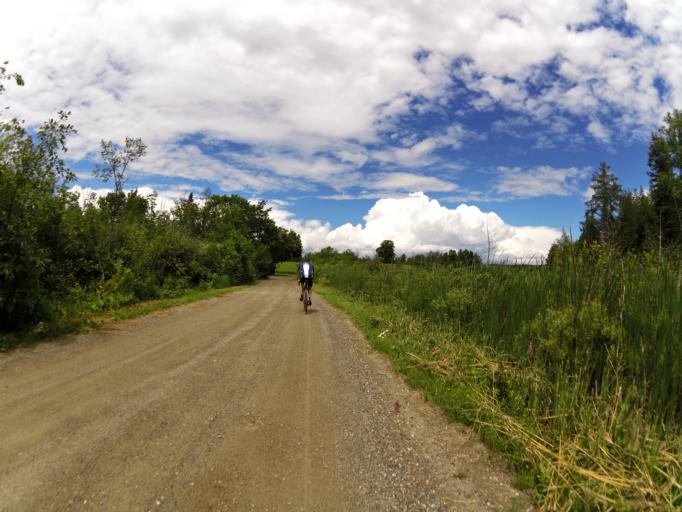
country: CA
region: Ontario
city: Renfrew
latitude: 45.1293
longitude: -76.6843
